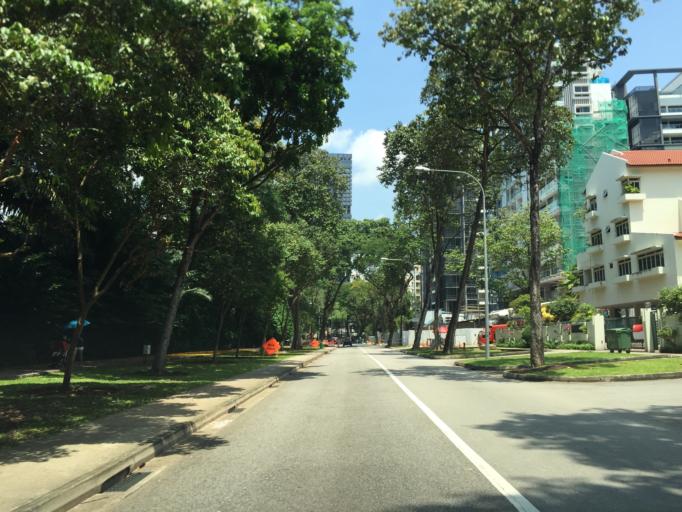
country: SG
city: Singapore
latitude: 1.3144
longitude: 103.8316
